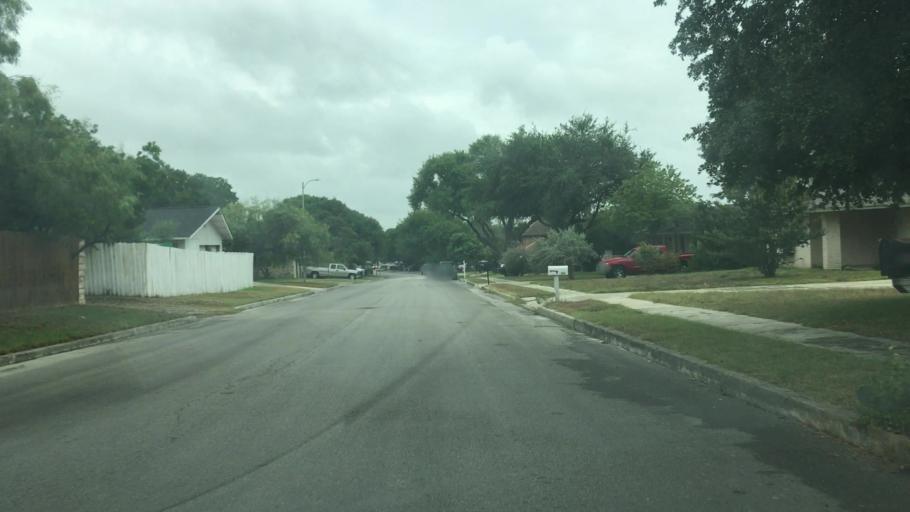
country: US
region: Texas
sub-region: Bexar County
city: Universal City
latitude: 29.5506
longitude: -98.3146
